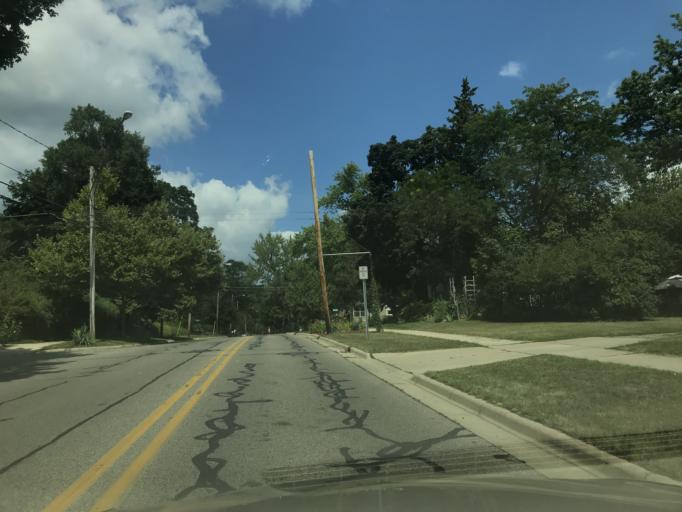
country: US
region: Michigan
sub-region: Jackson County
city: Jackson
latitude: 42.2345
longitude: -84.4184
